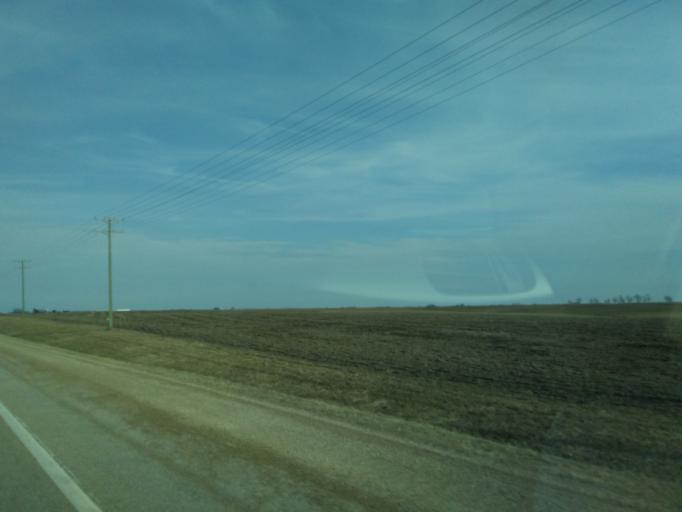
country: US
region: Wisconsin
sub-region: Grant County
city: Lancaster
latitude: 42.9653
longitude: -90.9024
